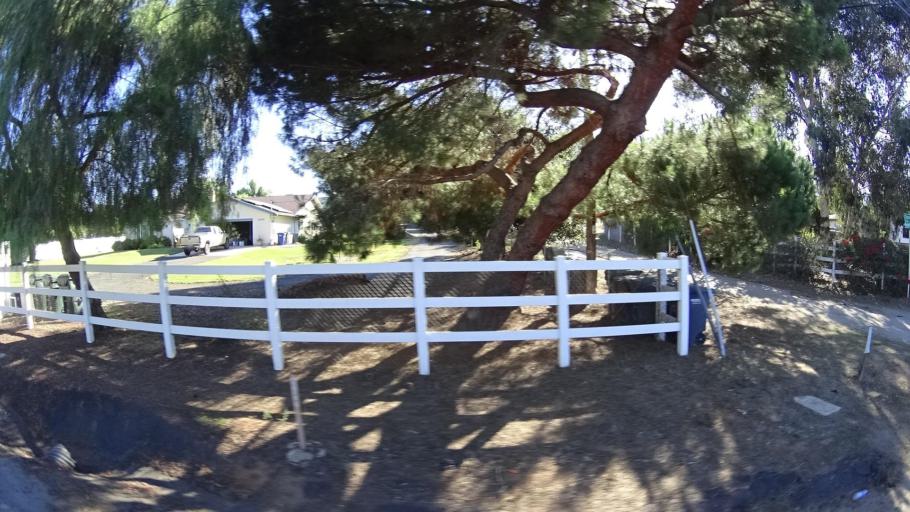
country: US
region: California
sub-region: San Diego County
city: Jamul
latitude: 32.7124
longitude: -116.8807
